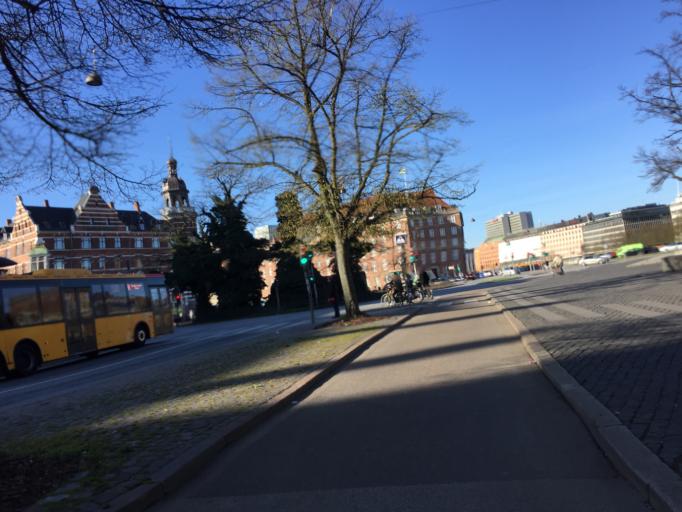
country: DK
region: Capital Region
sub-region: Kobenhavn
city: Copenhagen
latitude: 55.6794
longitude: 12.5661
